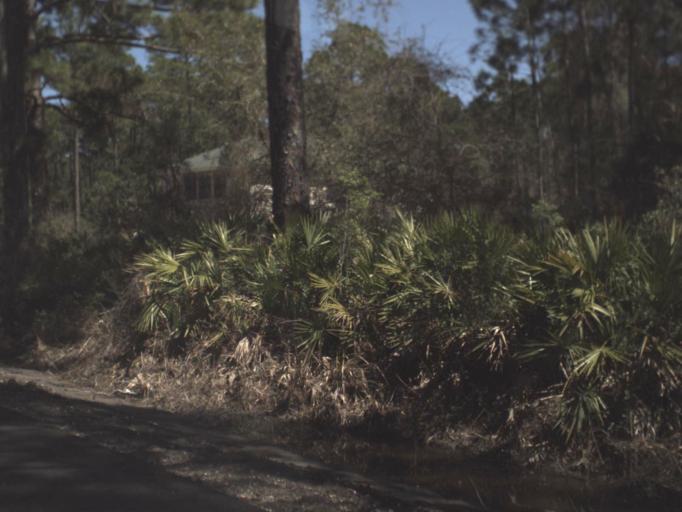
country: US
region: Florida
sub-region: Gulf County
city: Port Saint Joe
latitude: 29.6959
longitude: -85.3075
